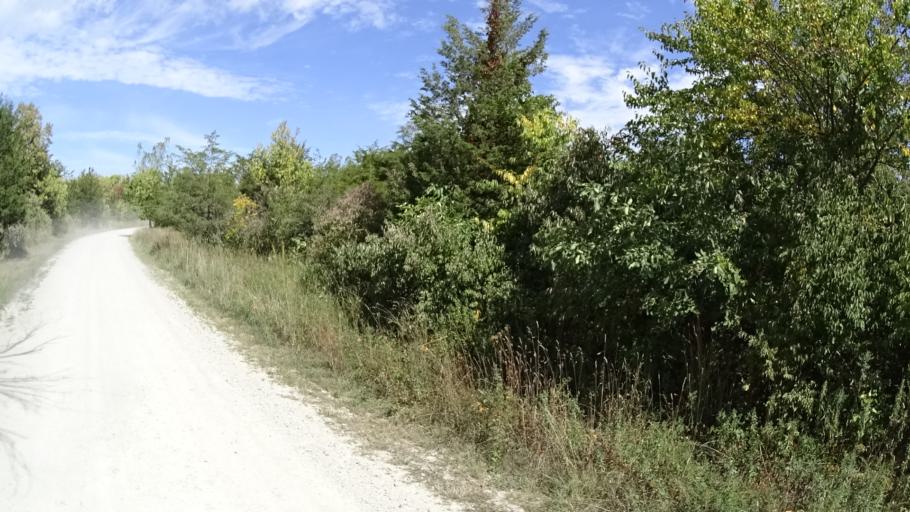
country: US
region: Ohio
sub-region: Erie County
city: Sandusky
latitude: 41.6031
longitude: -82.7200
